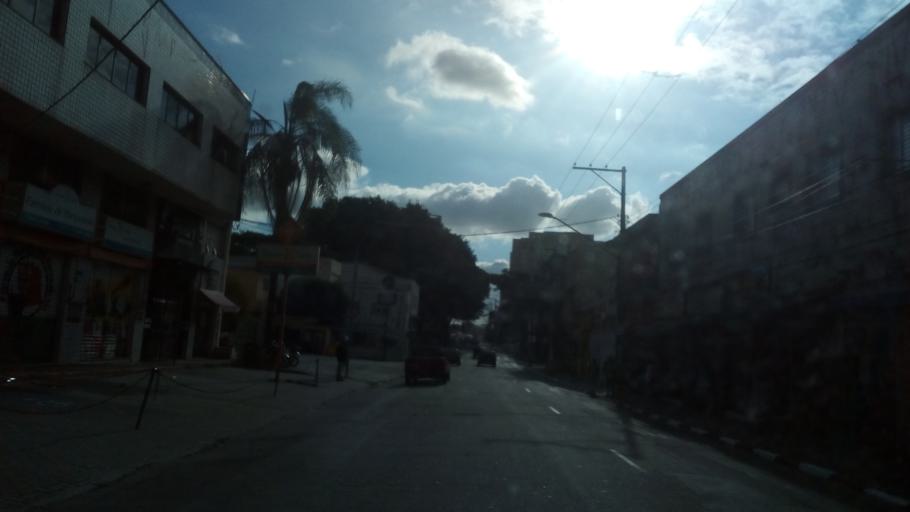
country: BR
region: Sao Paulo
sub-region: Guarulhos
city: Guarulhos
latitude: -23.4603
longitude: -46.5341
